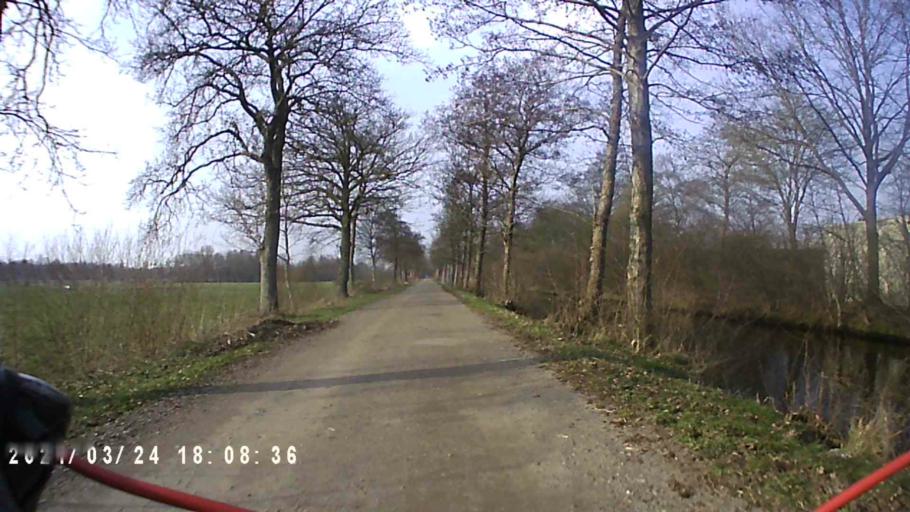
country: NL
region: Groningen
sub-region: Gemeente Leek
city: Leek
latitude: 53.1498
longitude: 6.3625
